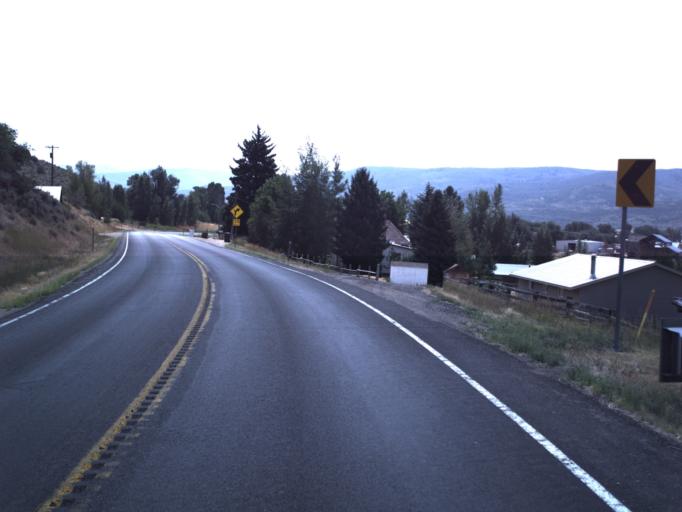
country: US
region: Utah
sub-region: Summit County
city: Francis
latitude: 40.5976
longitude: -111.2441
